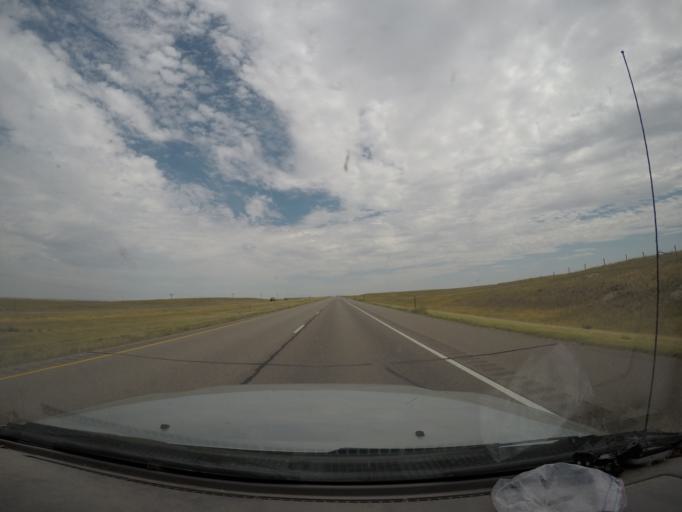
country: US
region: Nebraska
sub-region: Kimball County
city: Kimball
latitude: 41.1971
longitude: -103.7504
